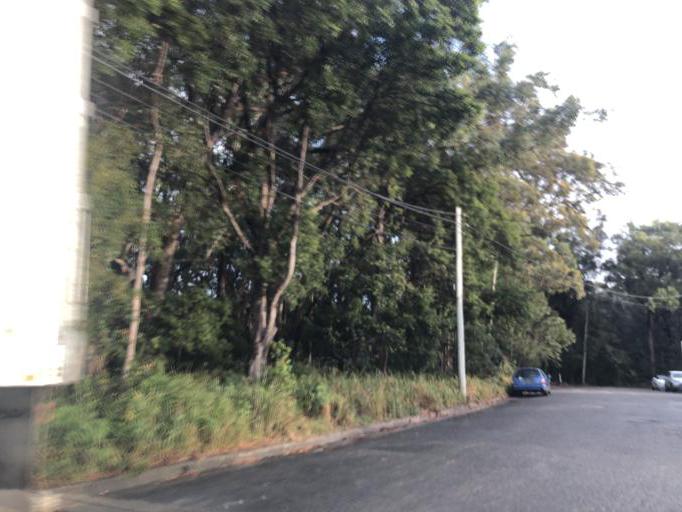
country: AU
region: New South Wales
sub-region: Coffs Harbour
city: Coffs Harbour
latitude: -30.2895
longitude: 153.1275
